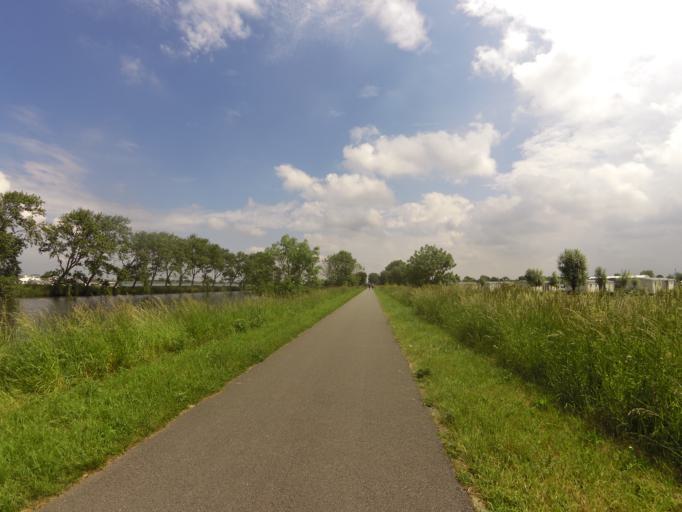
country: BE
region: Flanders
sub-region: Provincie West-Vlaanderen
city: Nieuwpoort
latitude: 51.1329
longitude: 2.7670
